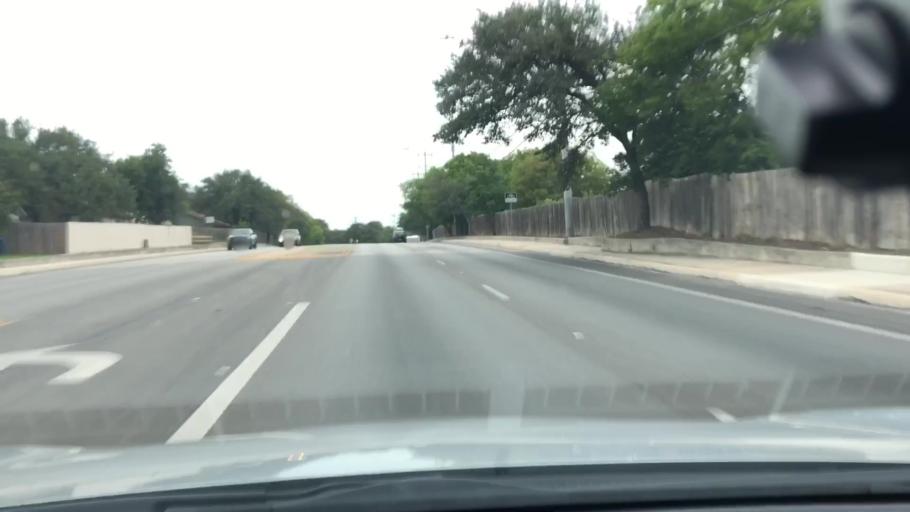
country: US
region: Texas
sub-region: Bexar County
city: Leon Valley
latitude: 29.4919
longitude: -98.6653
